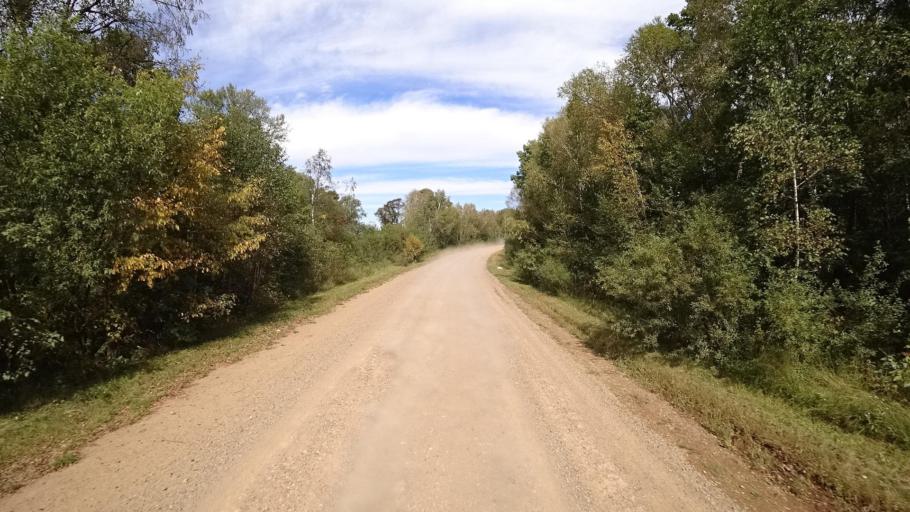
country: RU
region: Primorskiy
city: Yakovlevka
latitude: 44.6941
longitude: 133.6192
